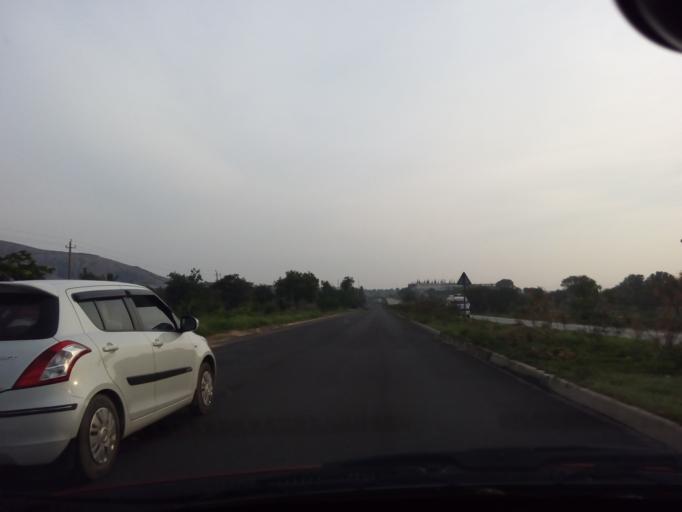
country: IN
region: Karnataka
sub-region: Chikkaballapur
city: Gudibanda
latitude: 13.6166
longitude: 77.7898
